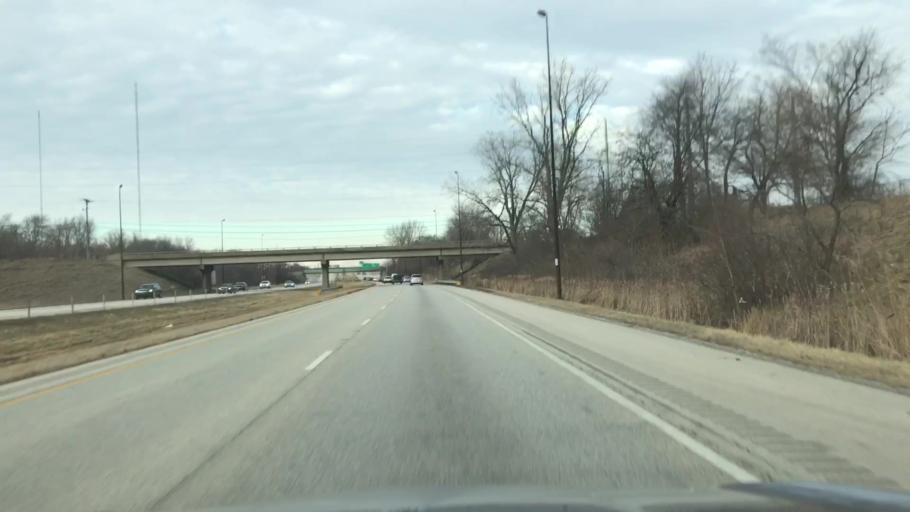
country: US
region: Illinois
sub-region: Sangamon County
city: Grandview
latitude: 39.8228
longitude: -89.5925
